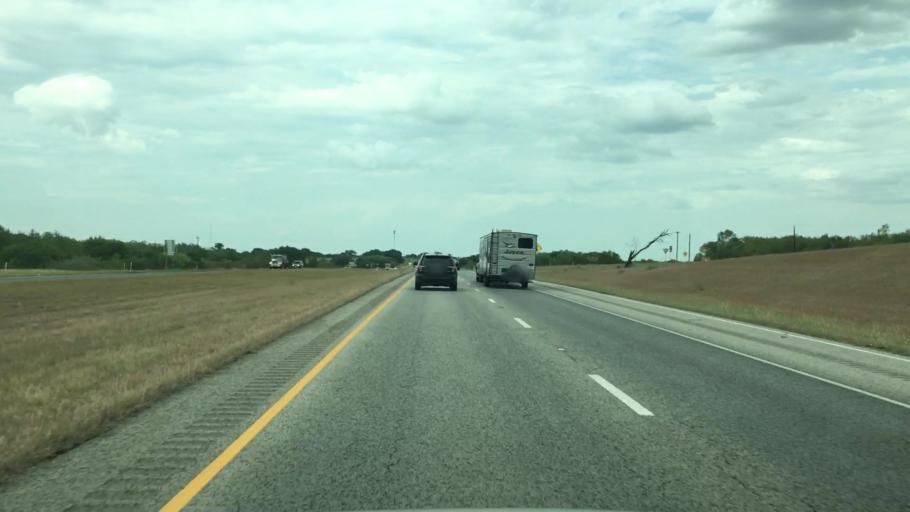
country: US
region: Texas
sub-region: Atascosa County
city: Pleasanton
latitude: 29.1075
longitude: -98.4322
